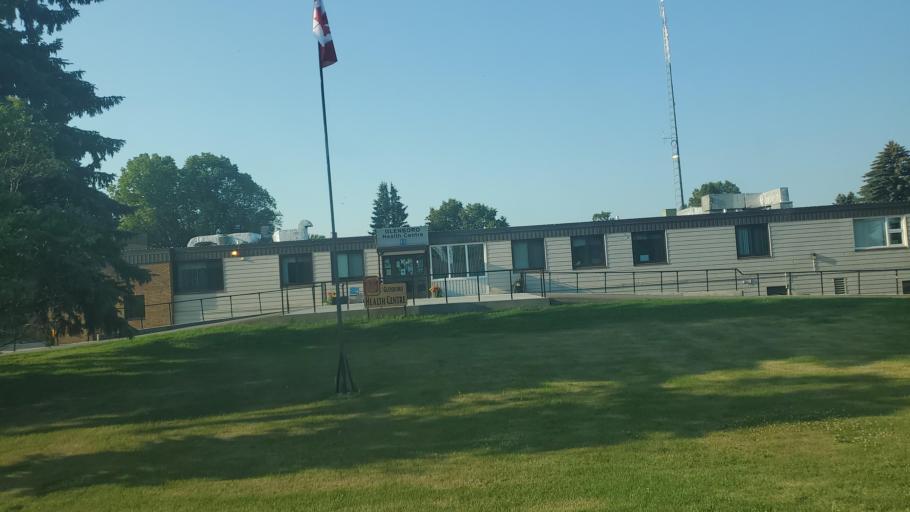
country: CA
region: Manitoba
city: Carberry
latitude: 49.5598
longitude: -99.2858
